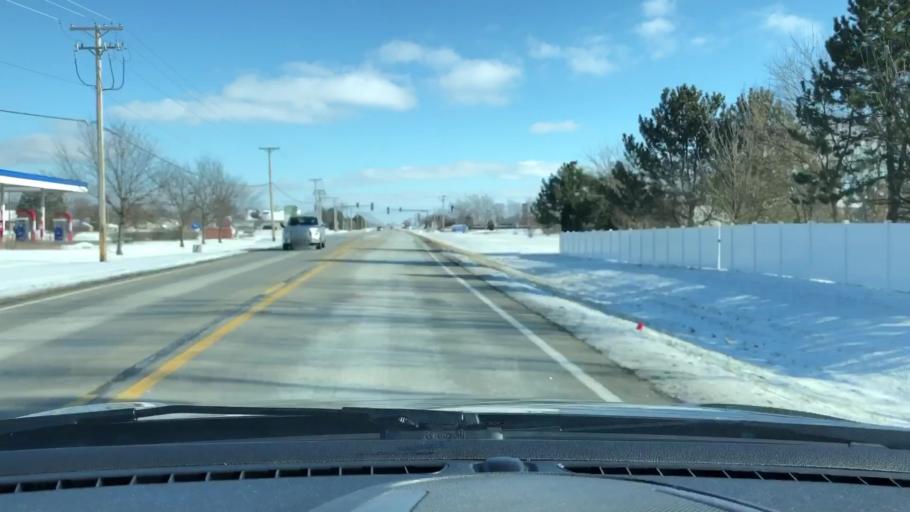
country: US
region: Illinois
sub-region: Will County
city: New Lenox
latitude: 41.4827
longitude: -87.9868
